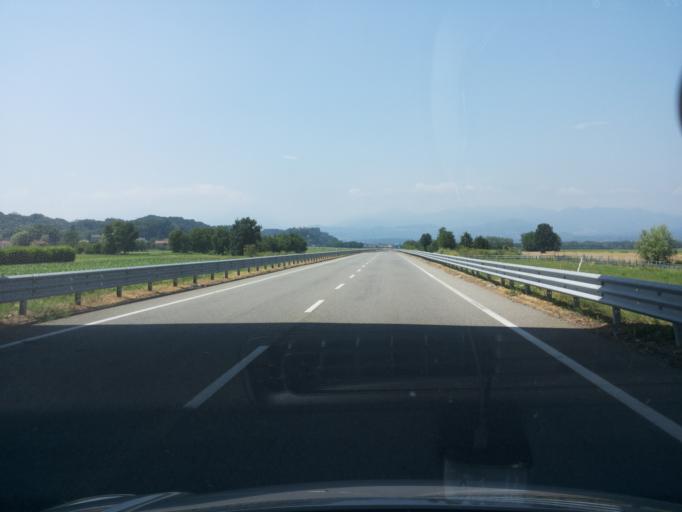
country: IT
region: Piedmont
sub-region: Provincia di Biella
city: Castelletto Cervo
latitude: 45.5184
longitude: 8.2077
